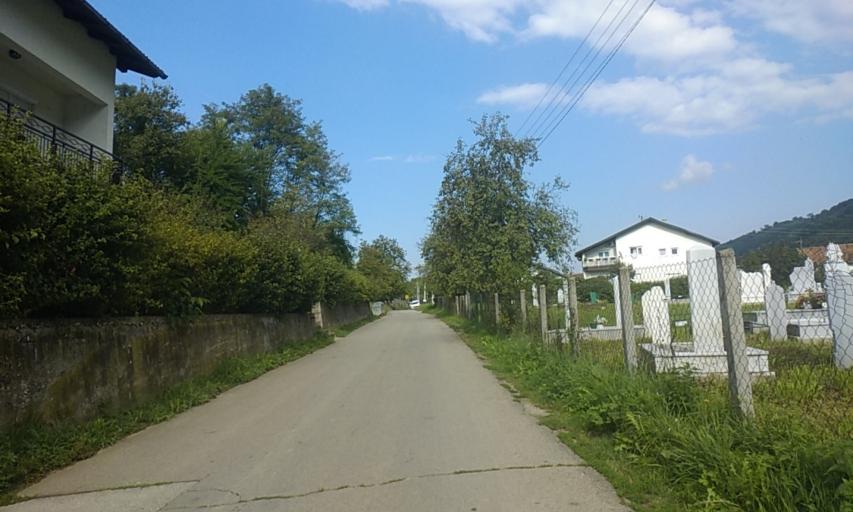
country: BA
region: Republika Srpska
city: Hiseti
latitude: 44.7524
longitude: 17.1673
